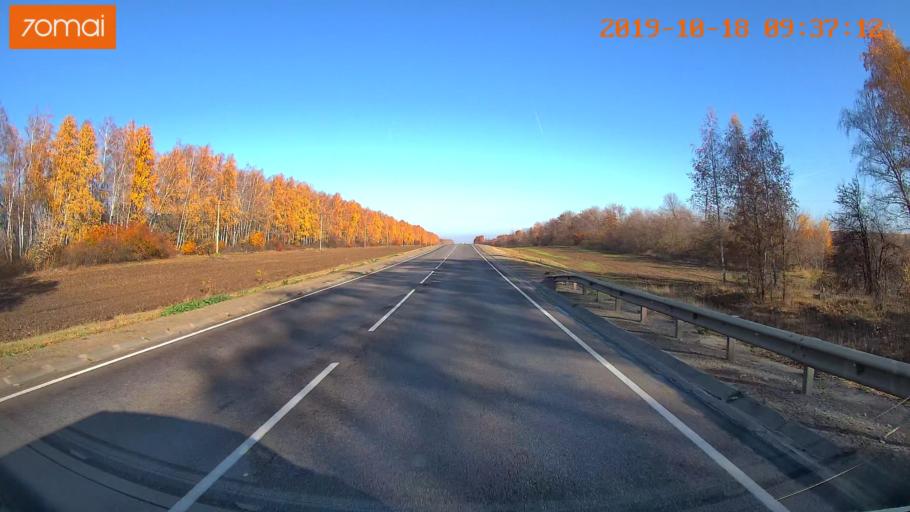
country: RU
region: Tula
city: Yefremov
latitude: 53.2184
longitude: 38.1420
